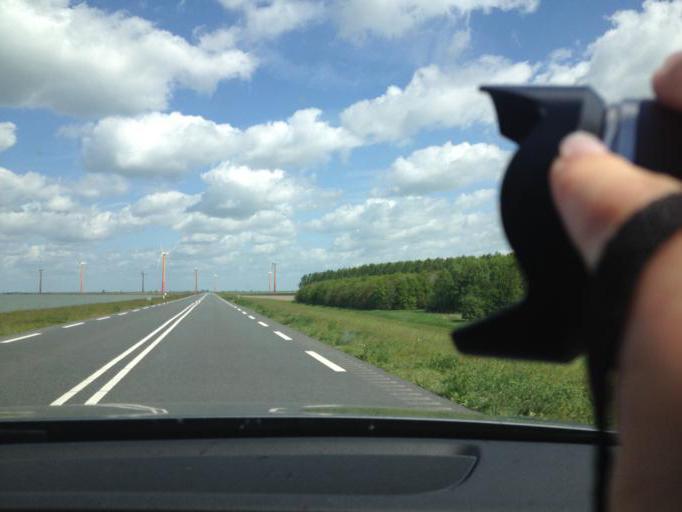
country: NL
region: North Holland
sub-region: Gemeente Naarden
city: Naarden
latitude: 52.3588
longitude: 5.1330
